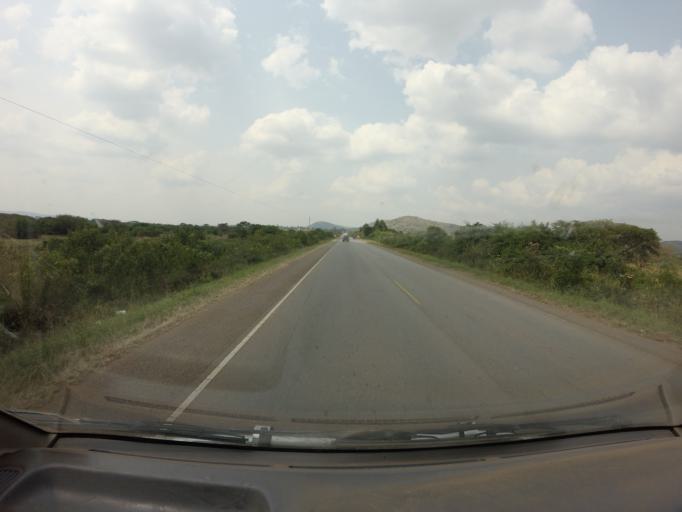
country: UG
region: Central Region
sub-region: Lyantonde District
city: Lyantonde
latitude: -0.3962
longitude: 31.1748
